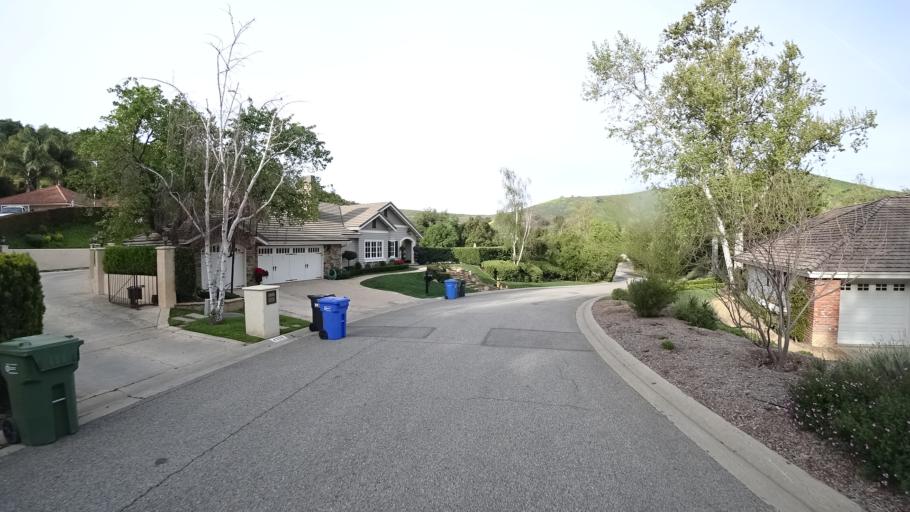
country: US
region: California
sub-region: Ventura County
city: Thousand Oaks
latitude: 34.1895
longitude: -118.8178
